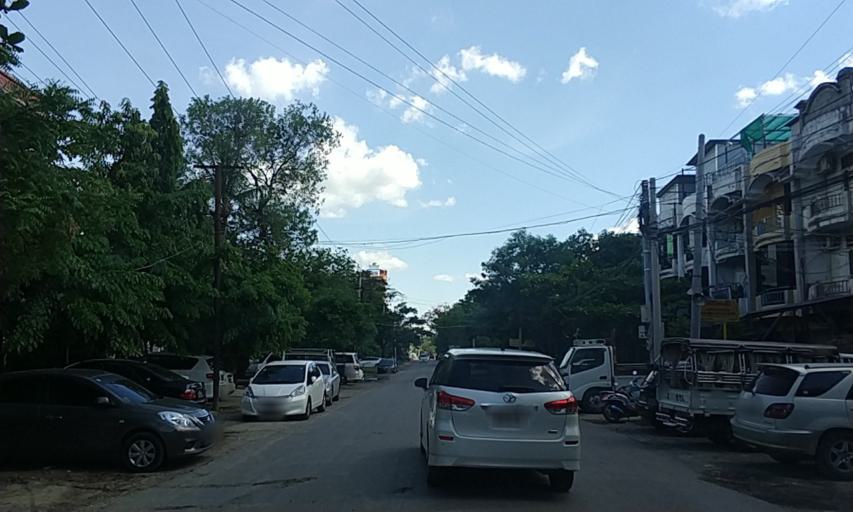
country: MM
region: Mandalay
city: Mandalay
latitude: 21.9755
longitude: 96.1079
